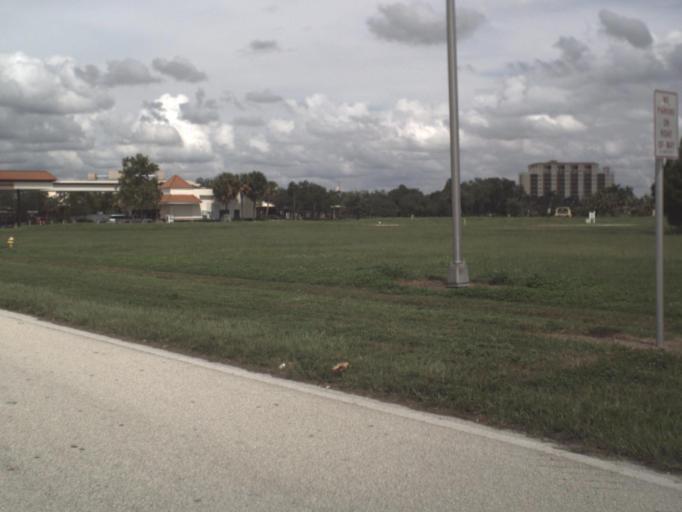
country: US
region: Florida
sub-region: Manatee County
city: Palmetto
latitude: 27.5122
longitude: -82.5630
